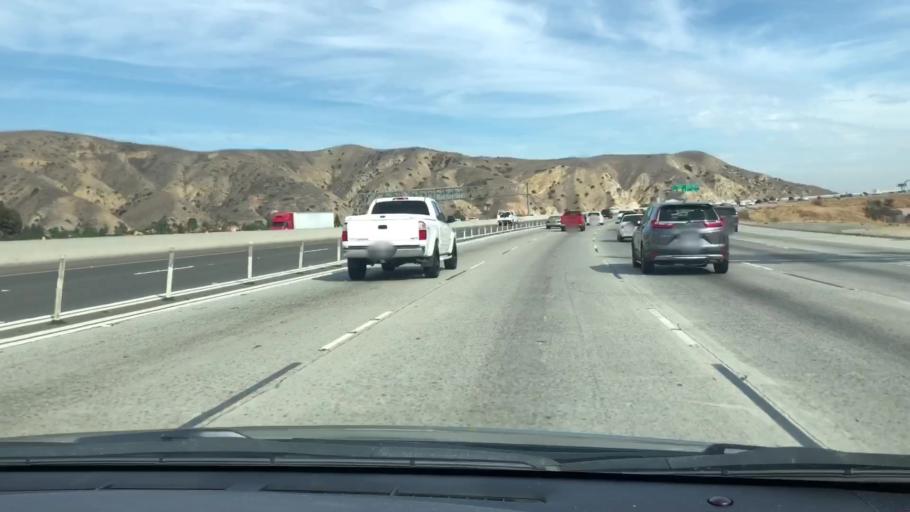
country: US
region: California
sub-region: San Bernardino County
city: Los Serranos
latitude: 33.8728
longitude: -117.6983
